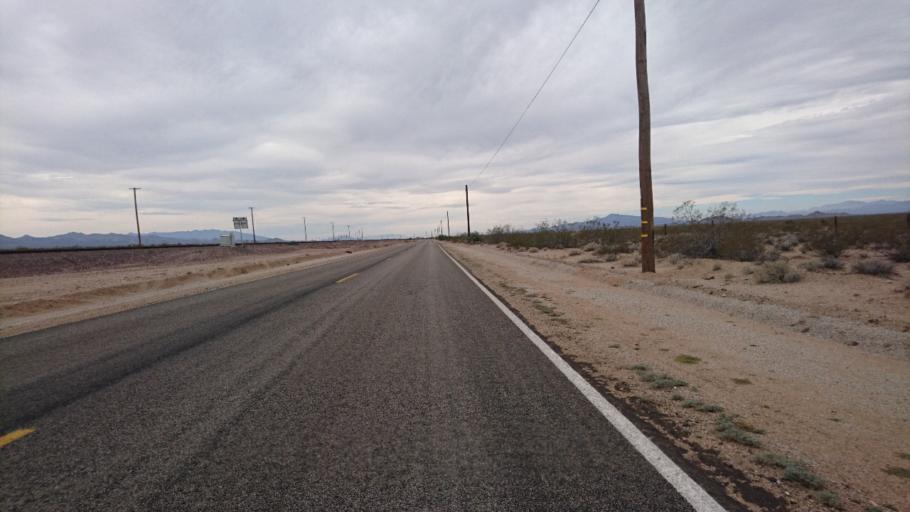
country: US
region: California
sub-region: San Bernardino County
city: Needles
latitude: 34.9025
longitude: -115.0884
